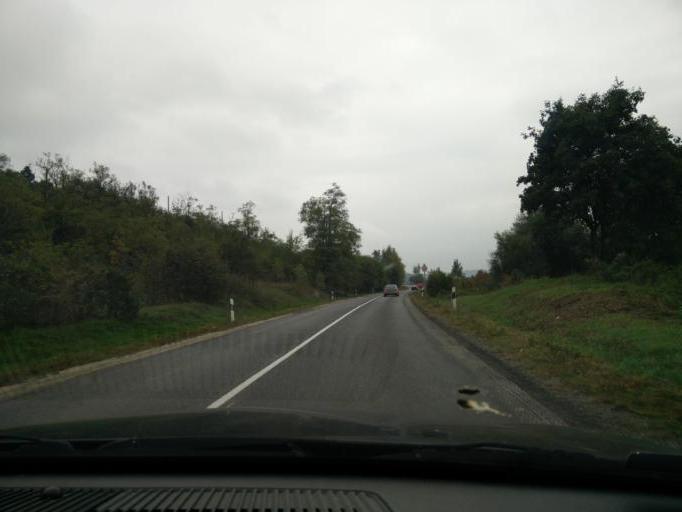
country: HU
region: Komarom-Esztergom
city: Piliscsev
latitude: 47.6668
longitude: 18.7811
